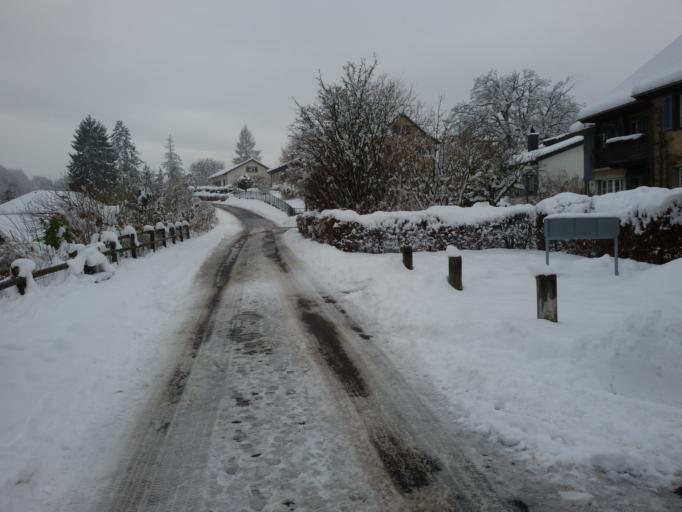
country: CH
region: Zurich
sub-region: Bezirk Hinwil
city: Rueti / Westlicher Dorfteil
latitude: 47.2557
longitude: 8.8407
